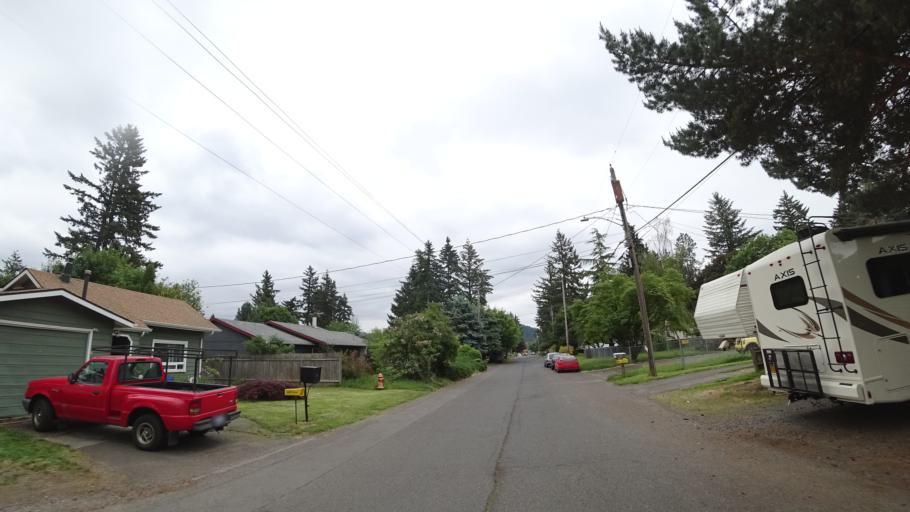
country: US
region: Oregon
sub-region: Multnomah County
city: Lents
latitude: 45.5081
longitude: -122.5156
